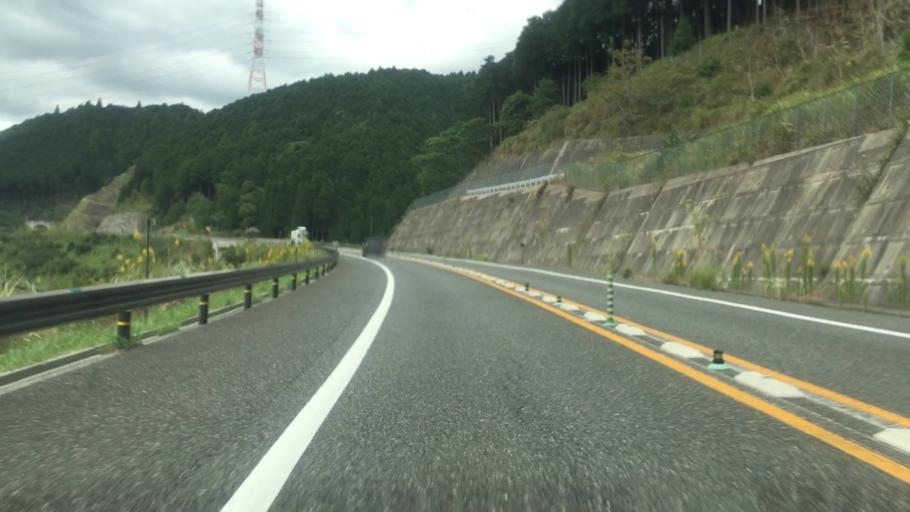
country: JP
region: Kyoto
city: Fukuchiyama
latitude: 35.2840
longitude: 134.9846
